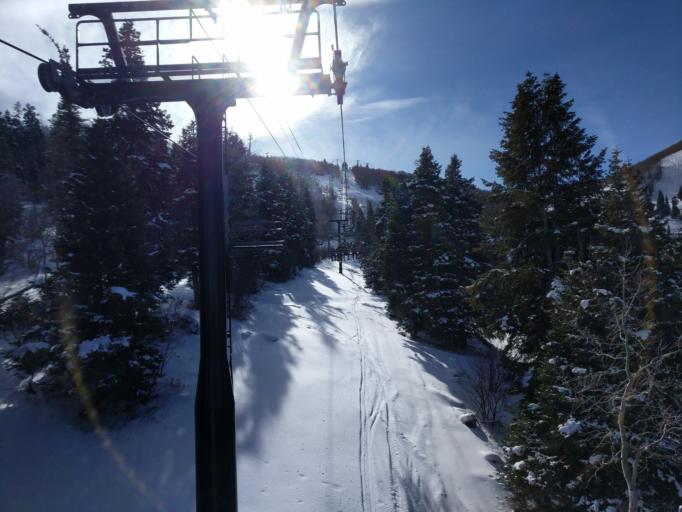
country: US
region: Utah
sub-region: Summit County
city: Park City
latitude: 40.6418
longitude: -111.5081
